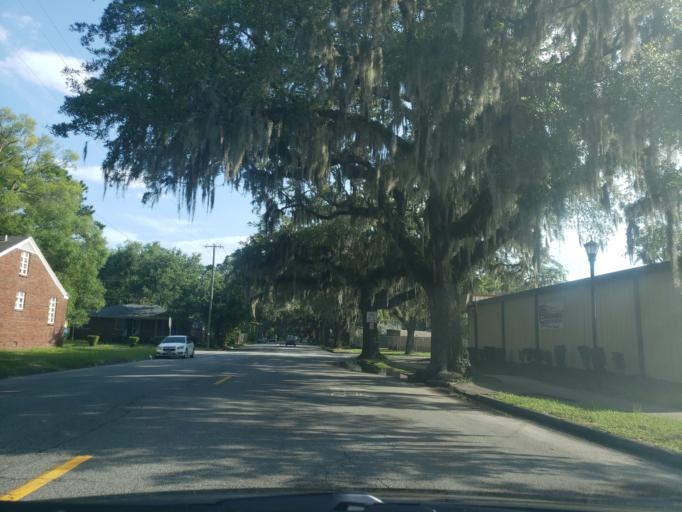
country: US
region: Georgia
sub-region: Chatham County
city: Savannah
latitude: 32.0491
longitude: -81.1055
